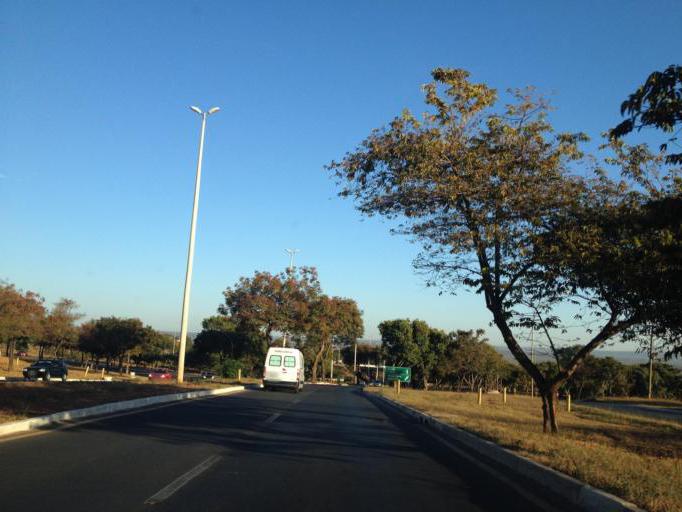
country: BR
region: Federal District
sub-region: Brasilia
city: Brasilia
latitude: -15.7589
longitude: -47.9251
